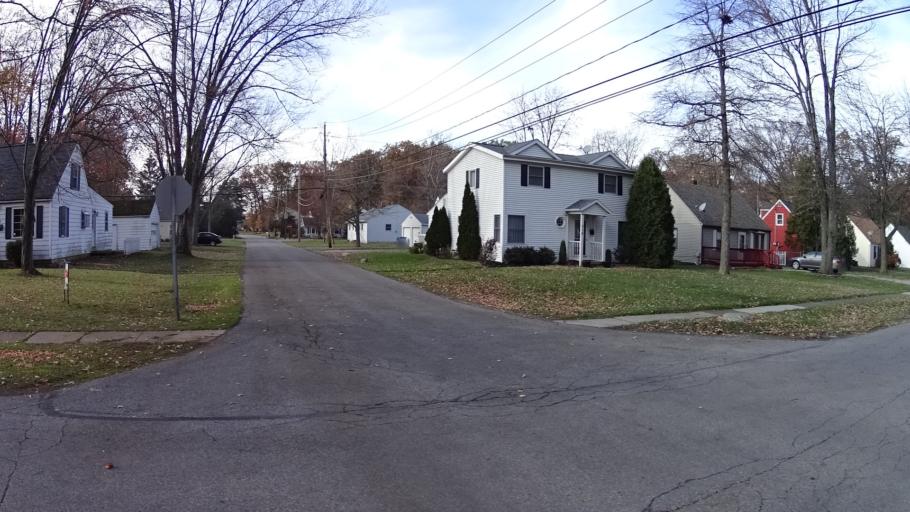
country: US
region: Ohio
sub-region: Lorain County
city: Avon Lake
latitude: 41.4997
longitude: -82.0250
